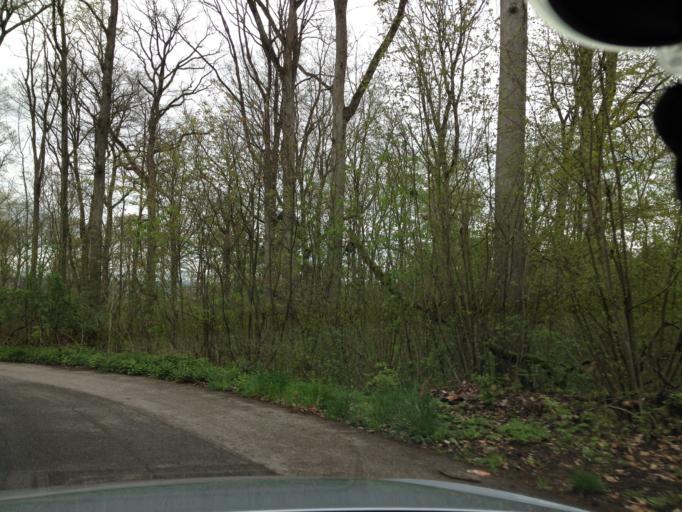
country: DE
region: Baden-Wuerttemberg
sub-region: Regierungsbezirk Stuttgart
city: Heilbronn
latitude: 49.1237
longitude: 9.2471
